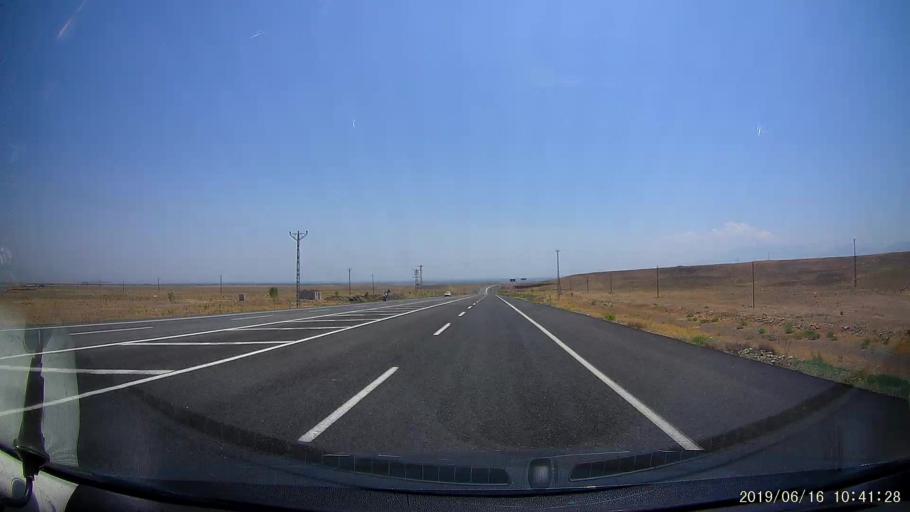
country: TR
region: Igdir
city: Tuzluca
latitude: 40.0474
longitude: 43.7834
